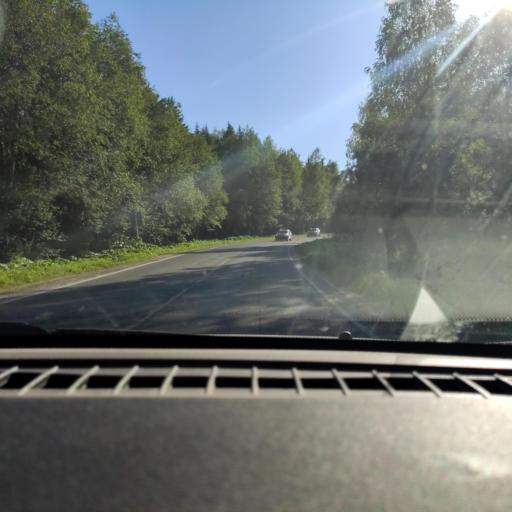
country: RU
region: Perm
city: Overyata
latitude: 58.1257
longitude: 55.8676
